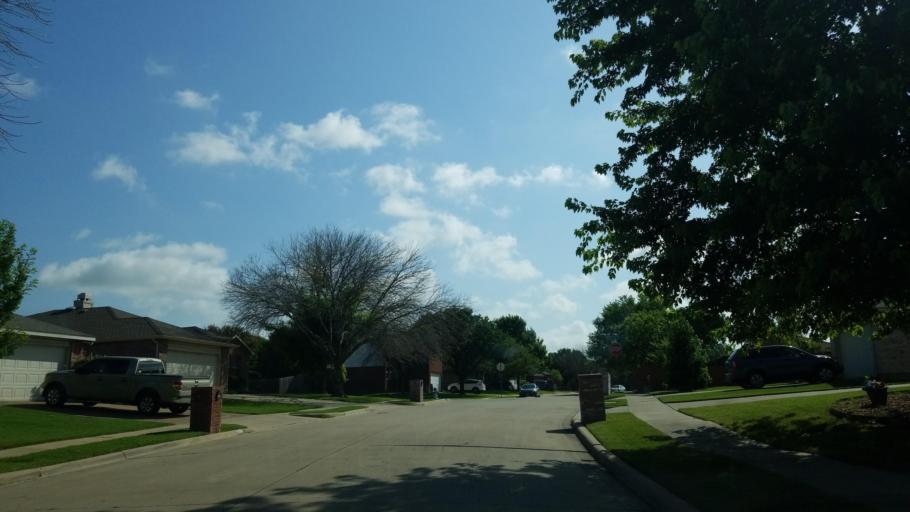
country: US
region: Texas
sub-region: Denton County
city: Copper Canyon
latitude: 33.1432
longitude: -97.1200
